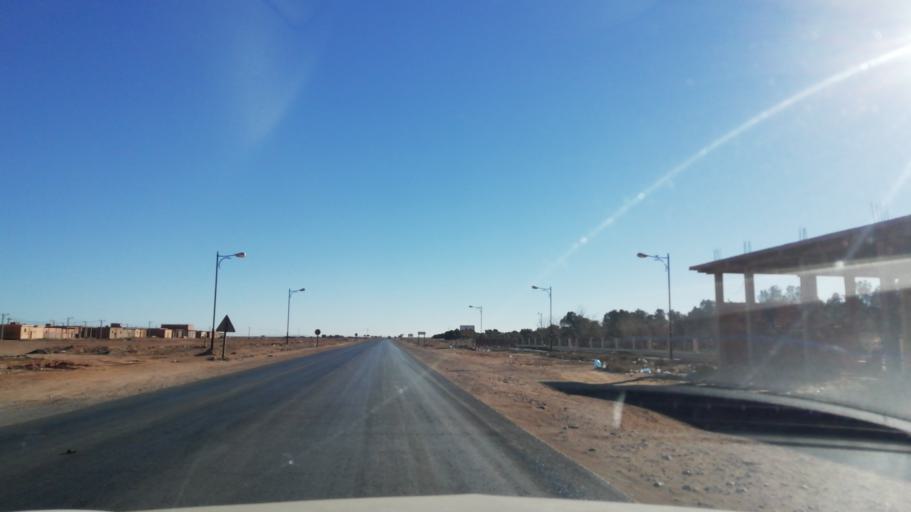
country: DZ
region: El Bayadh
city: El Bayadh
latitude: 33.8524
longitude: 0.6482
